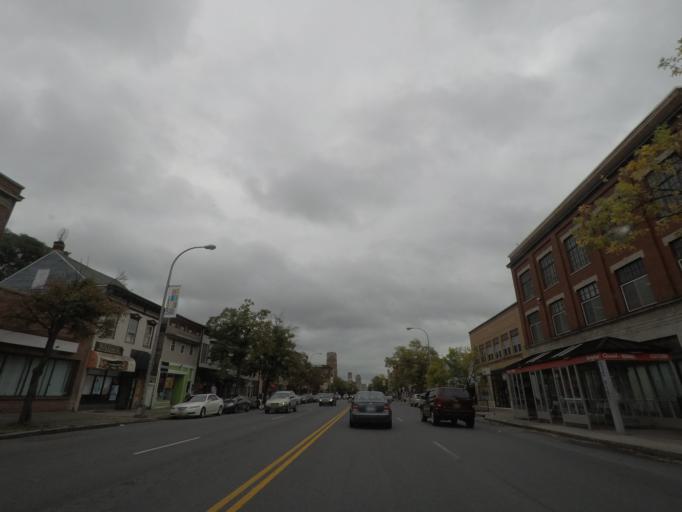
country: US
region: New York
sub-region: Albany County
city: West Albany
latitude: 42.6654
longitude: -73.7733
